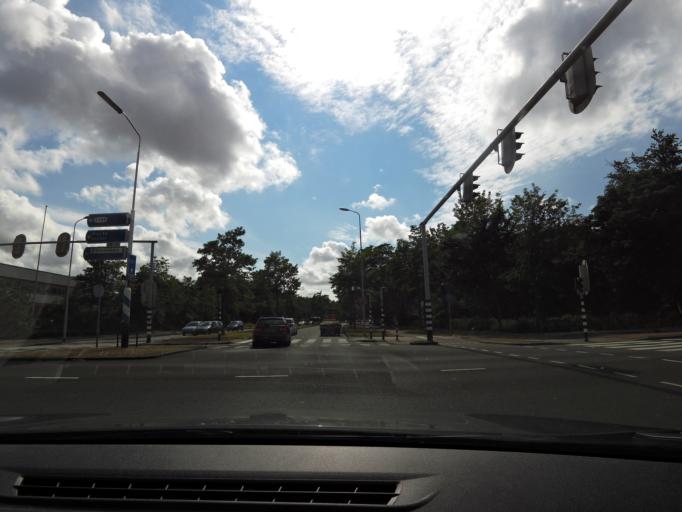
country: NL
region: South Holland
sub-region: Gemeente Rijswijk
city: Rijswijk
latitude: 52.0384
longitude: 4.3111
